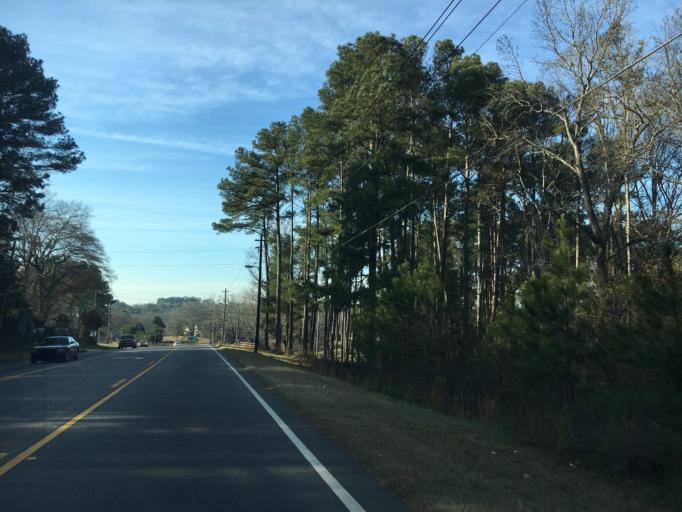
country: US
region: Georgia
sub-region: Hart County
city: Hartwell
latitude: 34.3596
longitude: -82.9483
